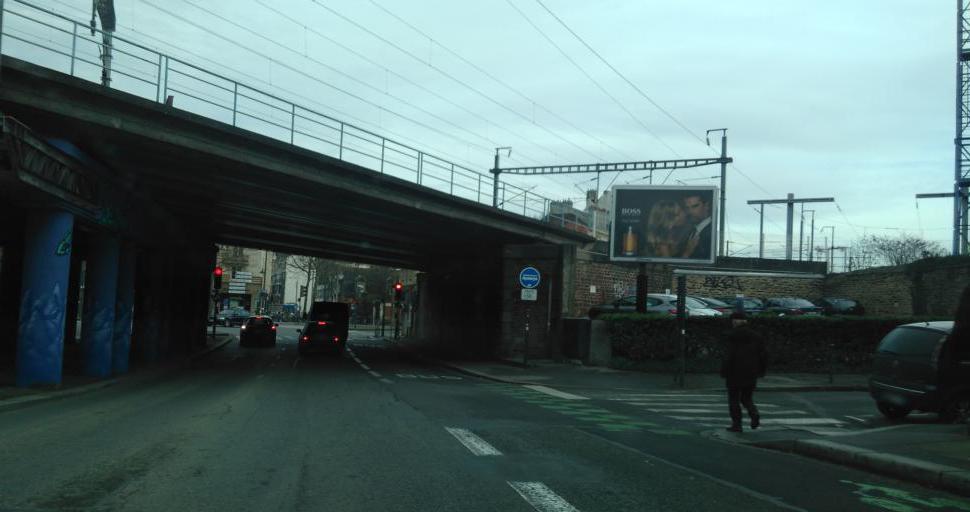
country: FR
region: Brittany
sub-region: Departement d'Ille-et-Vilaine
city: Rennes
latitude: 48.1014
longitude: -1.6847
